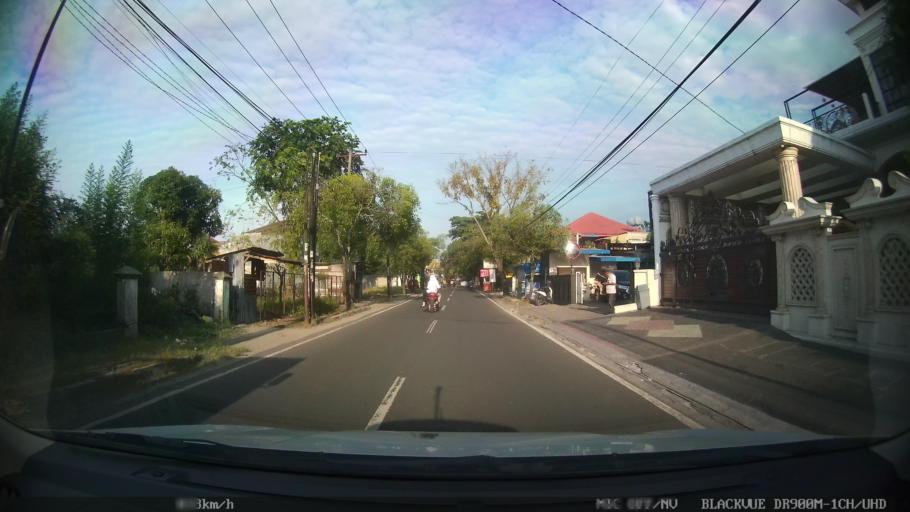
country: ID
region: North Sumatra
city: Medan
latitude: 3.5771
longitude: 98.6491
